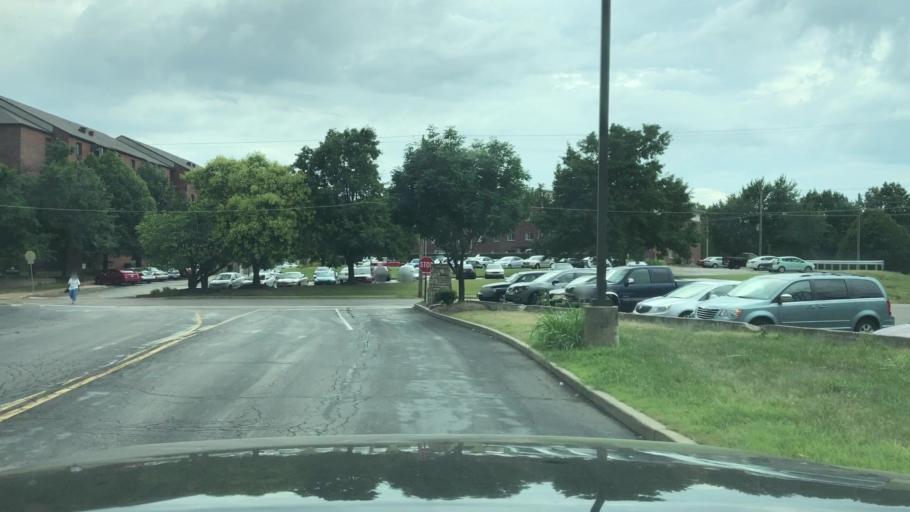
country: US
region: Missouri
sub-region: Saint Charles County
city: Saint Charles
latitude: 38.7730
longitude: -90.4986
